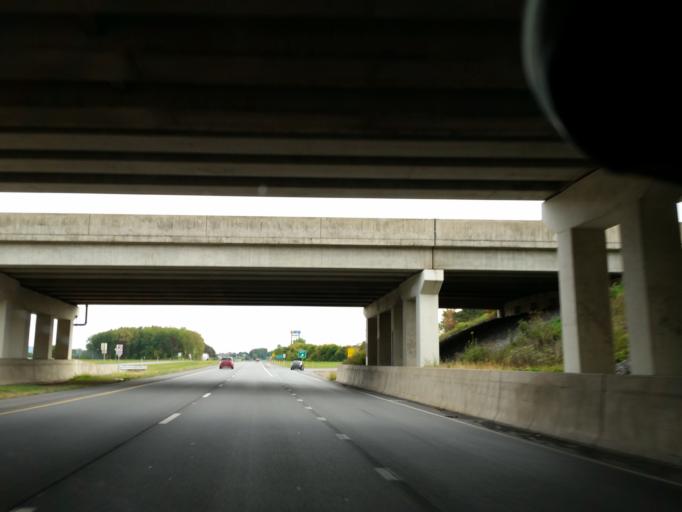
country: US
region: Pennsylvania
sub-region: Union County
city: New Columbia
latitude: 41.0525
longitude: -76.8719
